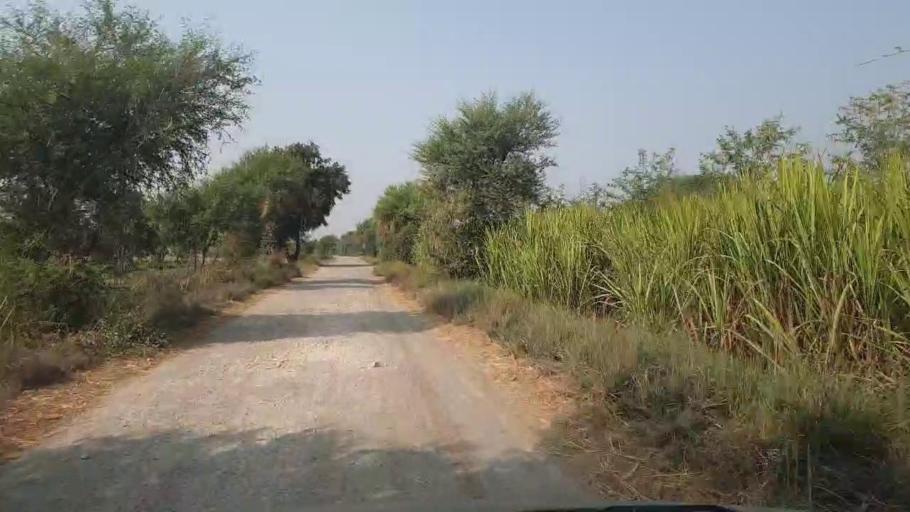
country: PK
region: Sindh
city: Tando Muhammad Khan
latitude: 25.0822
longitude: 68.3423
